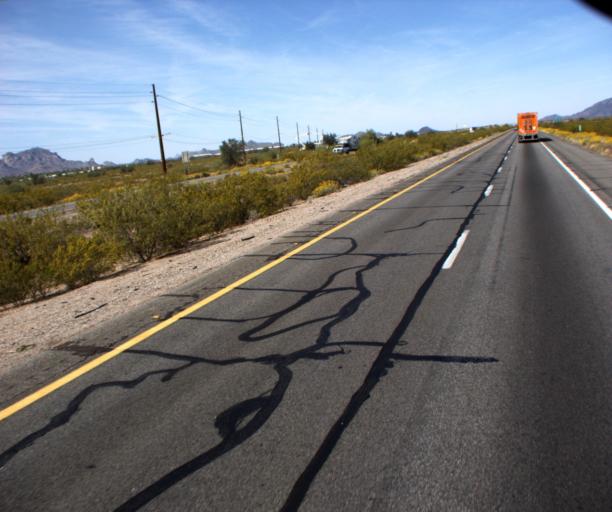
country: US
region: Arizona
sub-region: Maricopa County
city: Buckeye
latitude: 33.4941
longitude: -112.9217
